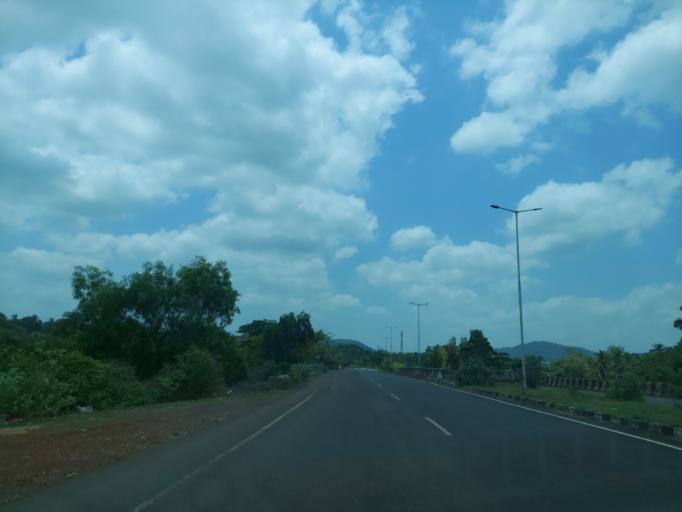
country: IN
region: Maharashtra
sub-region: Sindhudurg
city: Savantvadi
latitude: 15.8218
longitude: 73.8588
